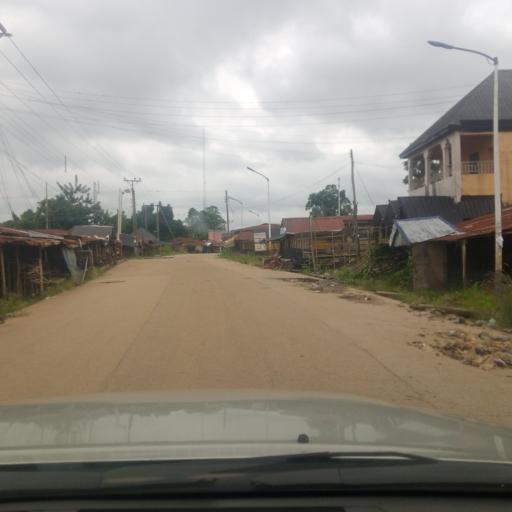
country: NG
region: Ebonyi
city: Effium
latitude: 6.6305
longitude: 8.0571
